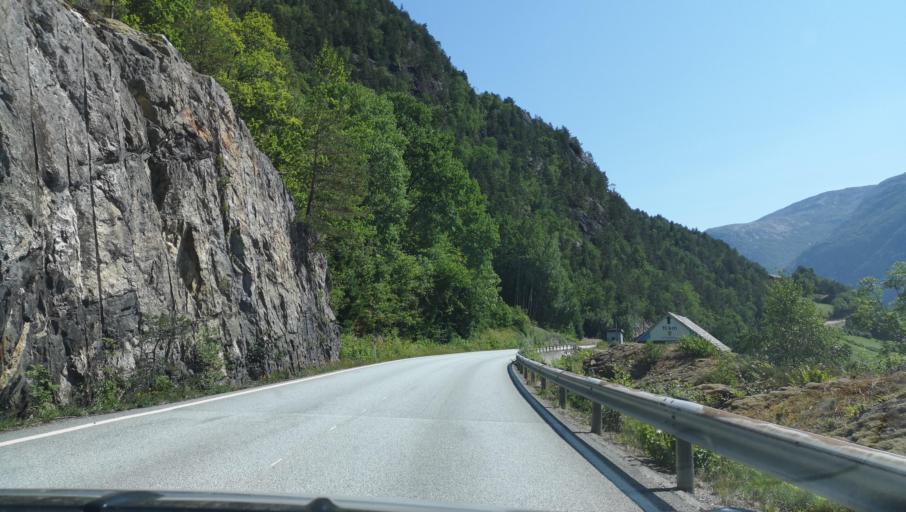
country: NO
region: Hordaland
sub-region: Ulvik
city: Ulvik
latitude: 60.4904
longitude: 6.8647
